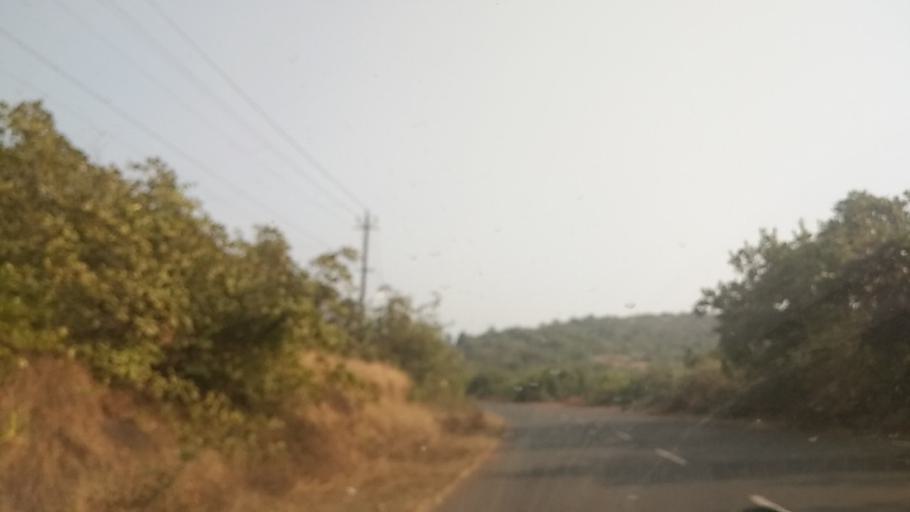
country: IN
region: Goa
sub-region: North Goa
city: Morjim
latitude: 15.6530
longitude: 73.7556
